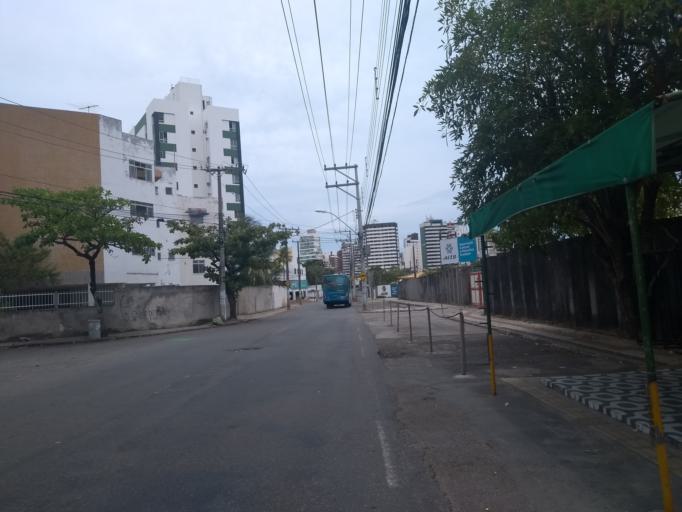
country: BR
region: Bahia
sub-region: Salvador
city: Salvador
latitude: -12.9935
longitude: -38.4488
